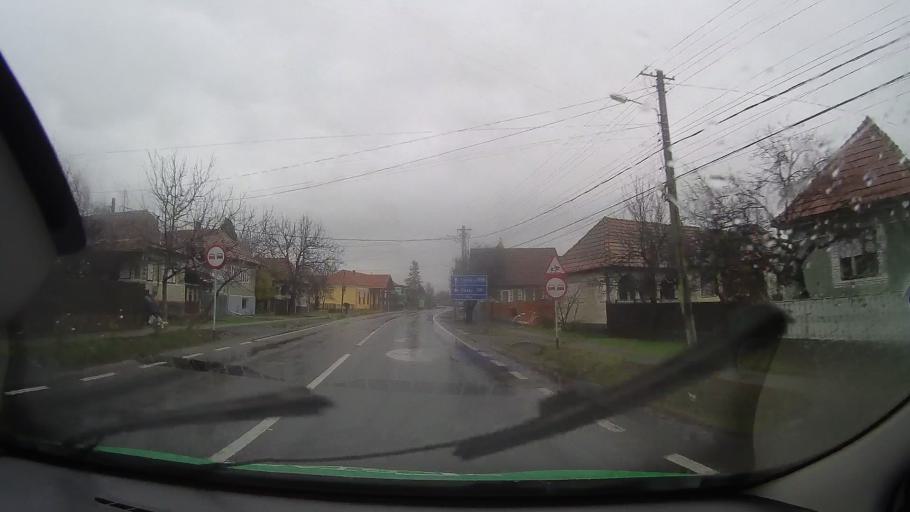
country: RO
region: Mures
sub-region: Comuna Brancovenesti
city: Valenii de Mures
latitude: 46.8896
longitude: 24.7959
